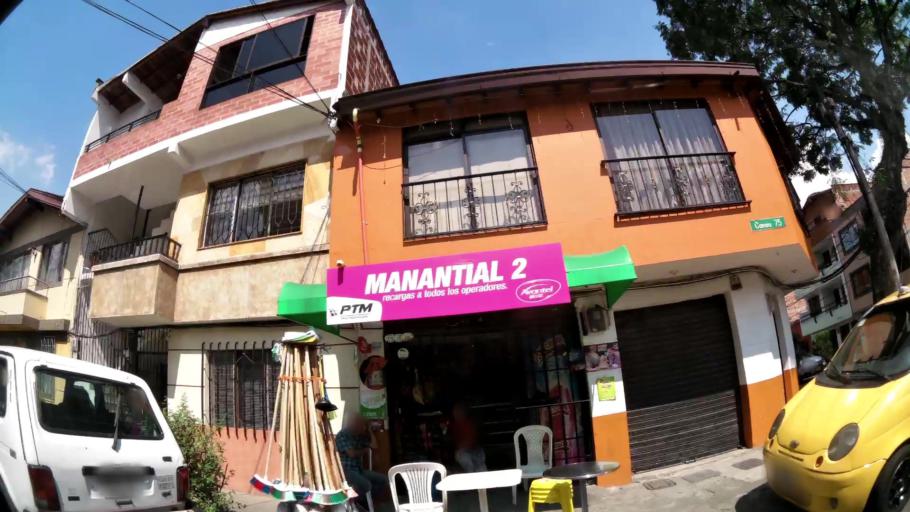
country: CO
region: Antioquia
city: Medellin
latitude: 6.2297
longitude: -75.5954
